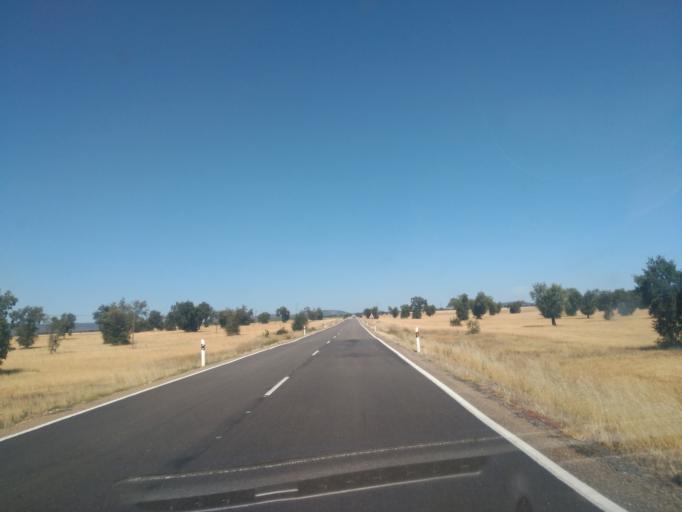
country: ES
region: Castille and Leon
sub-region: Provincia de Zamora
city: Pozuelo de Tabara
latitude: 41.7924
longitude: -5.9061
